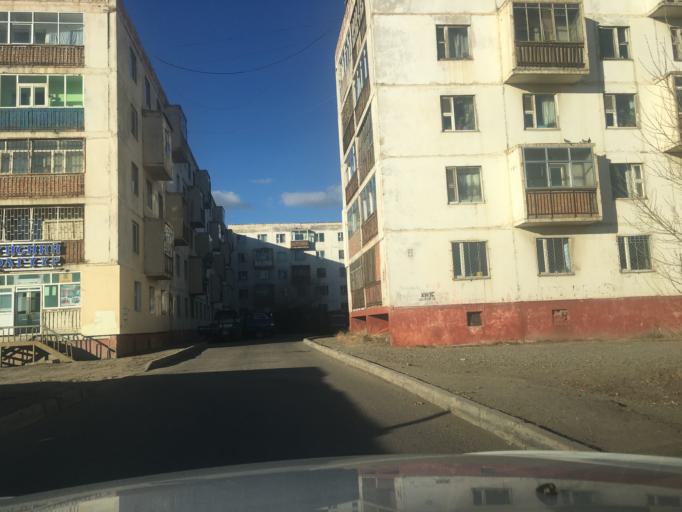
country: MN
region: Ulaanbaatar
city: Ulaanbaatar
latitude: 47.9104
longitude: 106.7772
